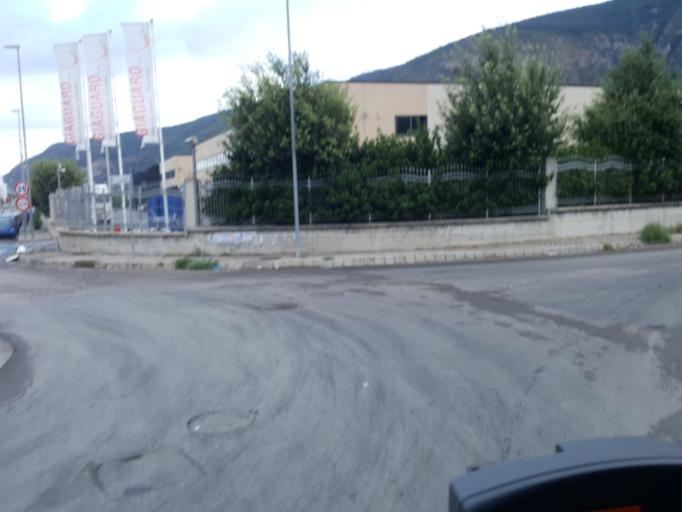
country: IT
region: Campania
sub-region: Provincia di Salerno
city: Sarno
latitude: 40.8201
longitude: 14.6014
